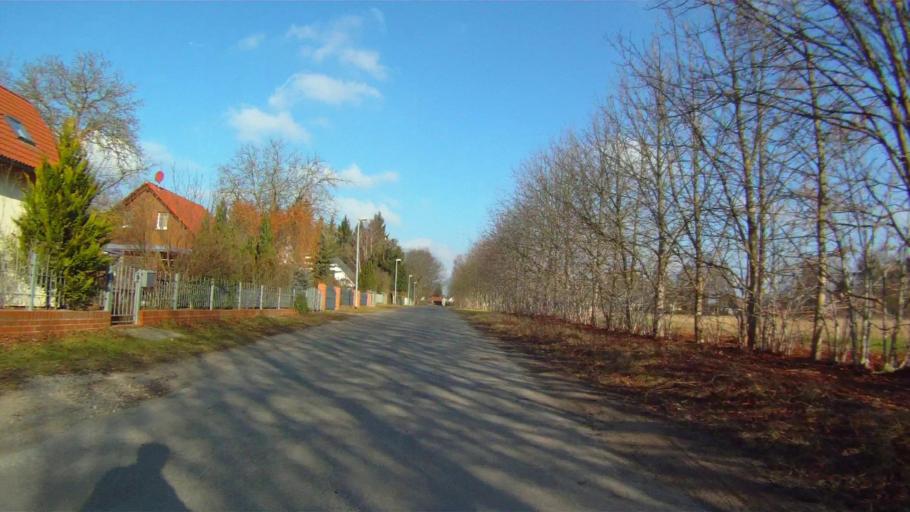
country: DE
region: Brandenburg
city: Schoneiche
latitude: 52.4702
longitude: 13.7156
